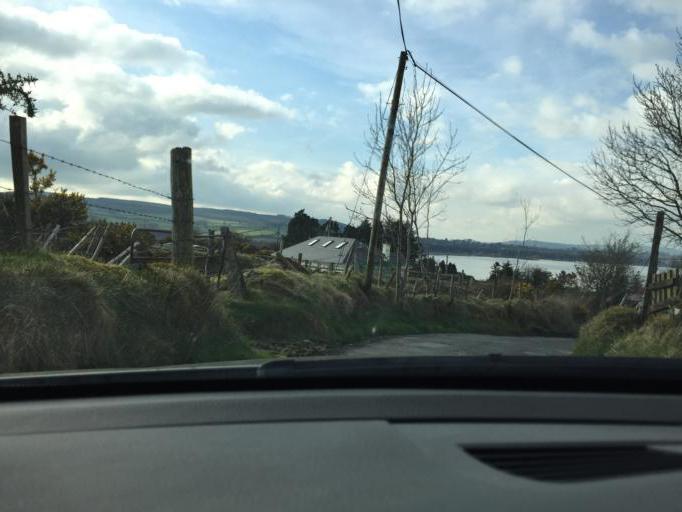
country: IE
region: Leinster
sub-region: Wicklow
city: Valleymount
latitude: 53.0935
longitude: -6.5247
